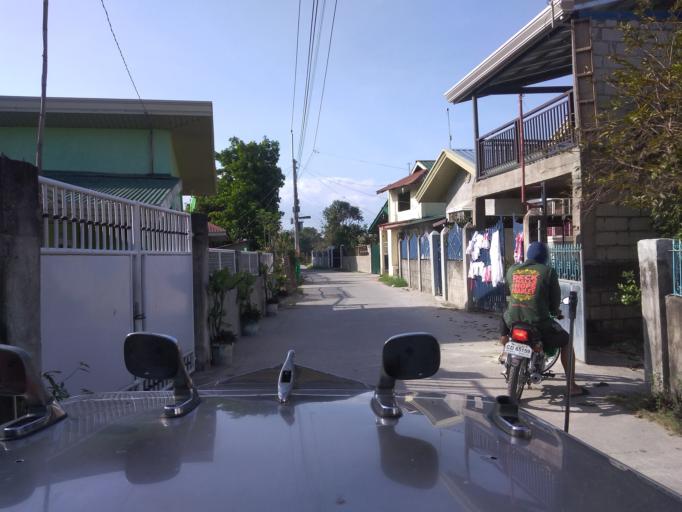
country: PH
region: Central Luzon
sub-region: Province of Pampanga
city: Bulaon
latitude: 15.0936
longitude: 120.6937
